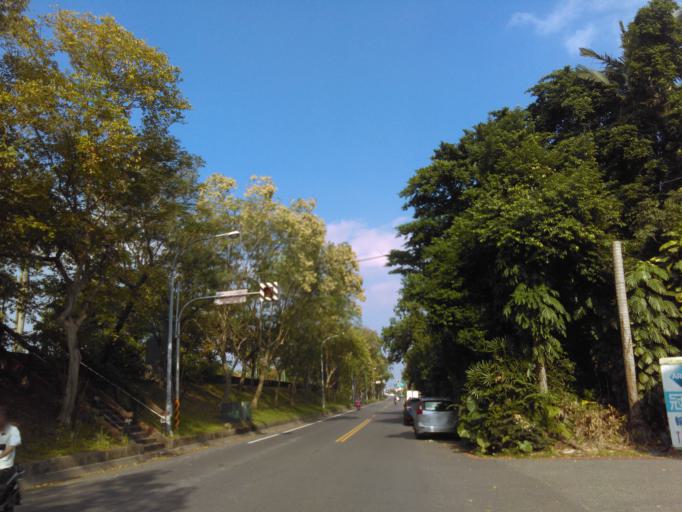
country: TW
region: Taiwan
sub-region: Yilan
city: Yilan
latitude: 24.7633
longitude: 121.7521
